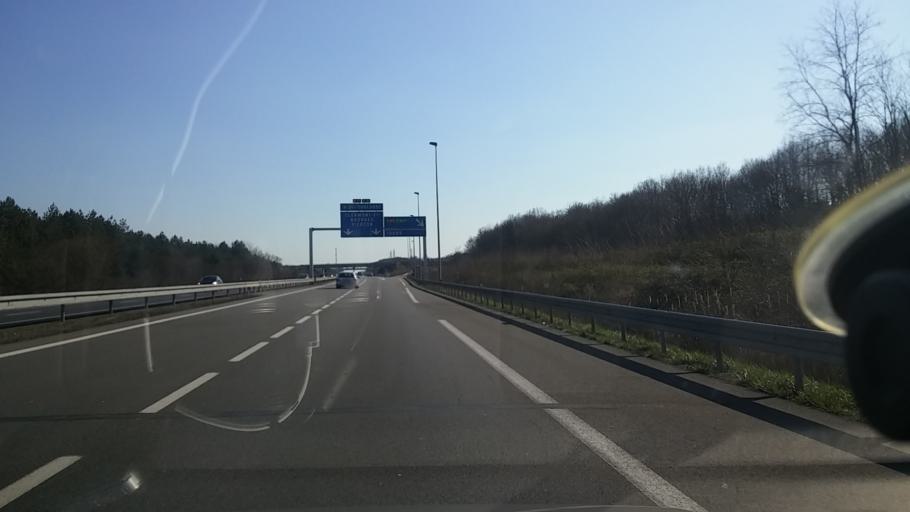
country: FR
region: Centre
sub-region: Departement du Loir-et-Cher
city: Theillay
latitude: 47.2941
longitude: 2.0441
